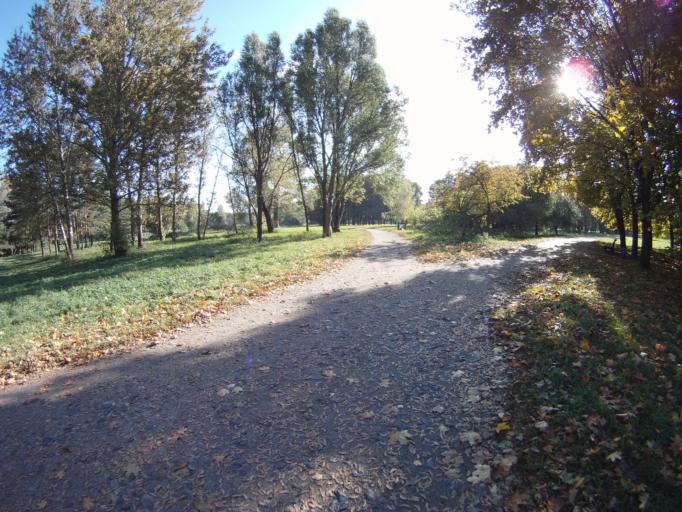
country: BY
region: Minsk
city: Minsk
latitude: 53.9355
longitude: 27.5702
